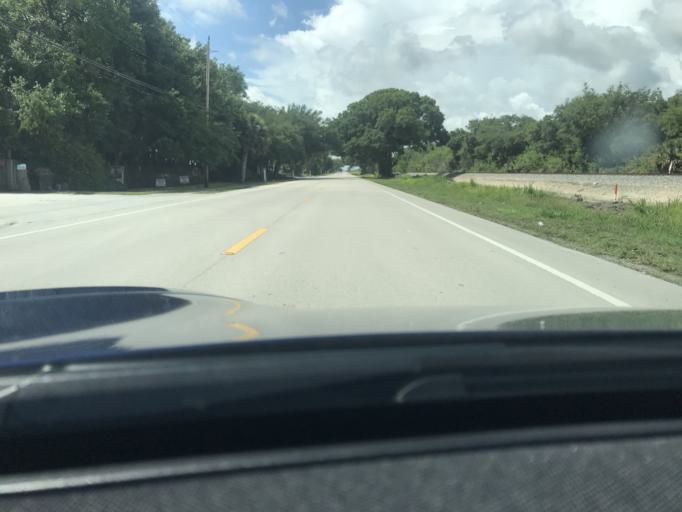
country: US
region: Florida
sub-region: Indian River County
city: Winter Beach
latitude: 27.7058
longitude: -80.4187
